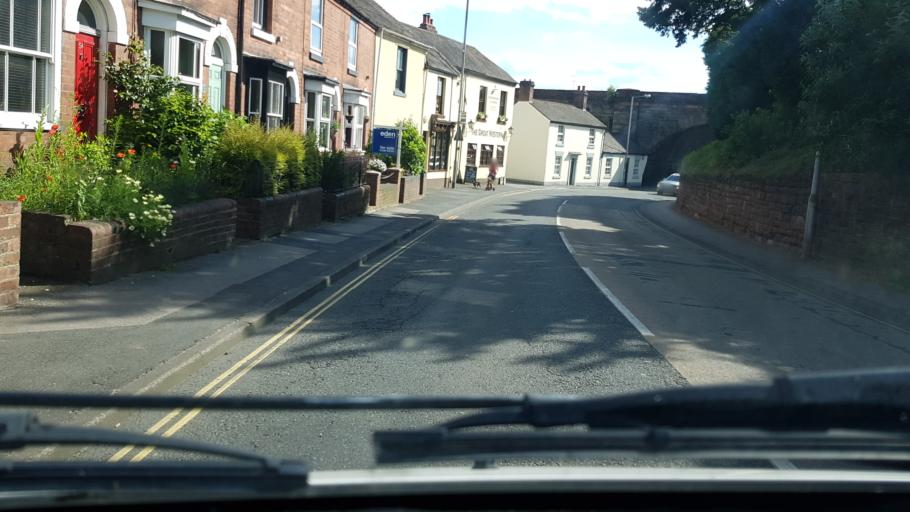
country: GB
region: England
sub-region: Worcestershire
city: Bewdley
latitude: 52.3772
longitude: -2.3083
